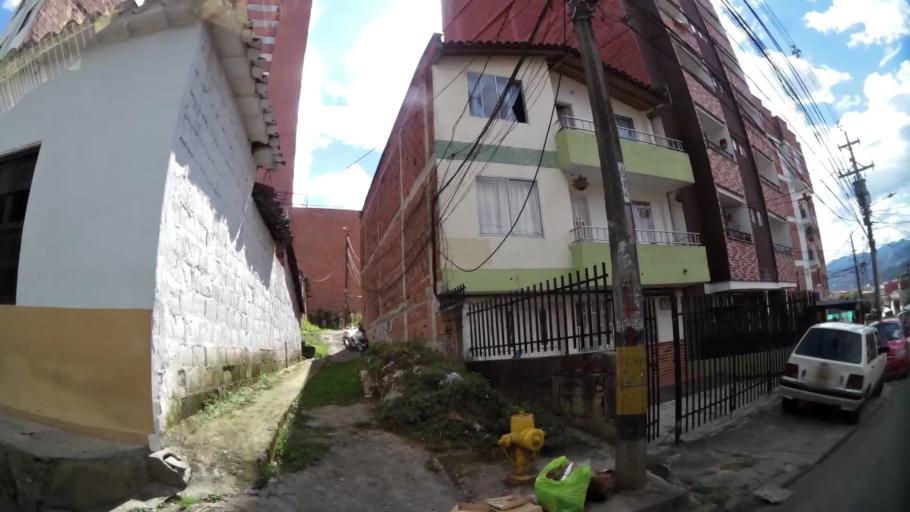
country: CO
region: Antioquia
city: Sabaneta
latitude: 6.1562
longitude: -75.6044
